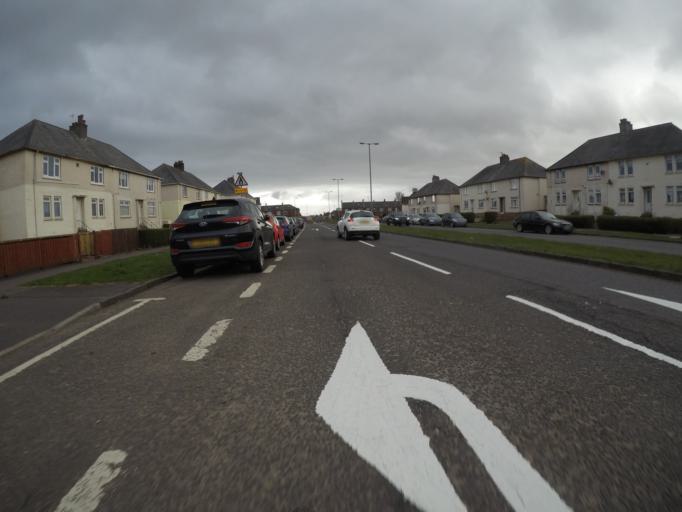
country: GB
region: Scotland
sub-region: East Ayrshire
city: Kilmarnock
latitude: 55.6141
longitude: -4.5146
